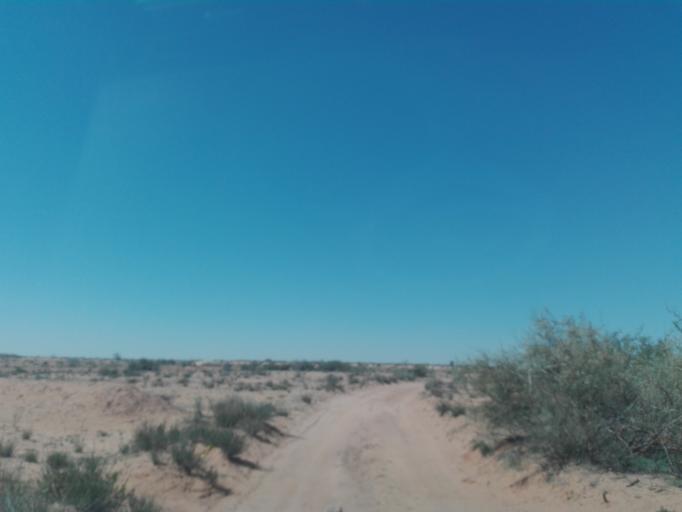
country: TN
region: Safaqis
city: Bi'r `Ali Bin Khalifah
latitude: 34.7898
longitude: 10.2735
